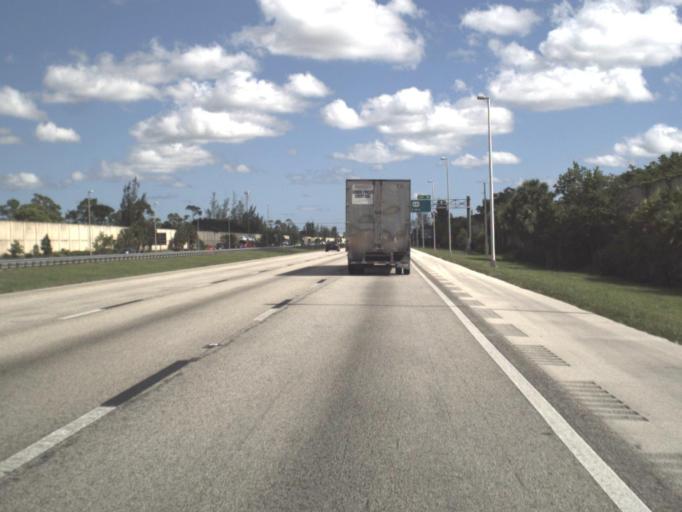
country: US
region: Florida
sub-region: Broward County
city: Parkland
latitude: 26.3005
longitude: -80.2254
